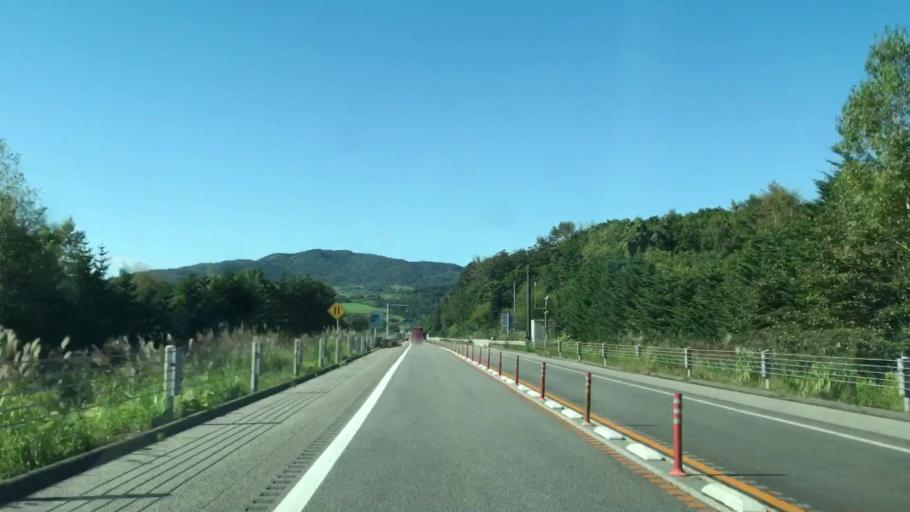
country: JP
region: Hokkaido
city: Date
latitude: 42.5344
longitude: 140.7984
